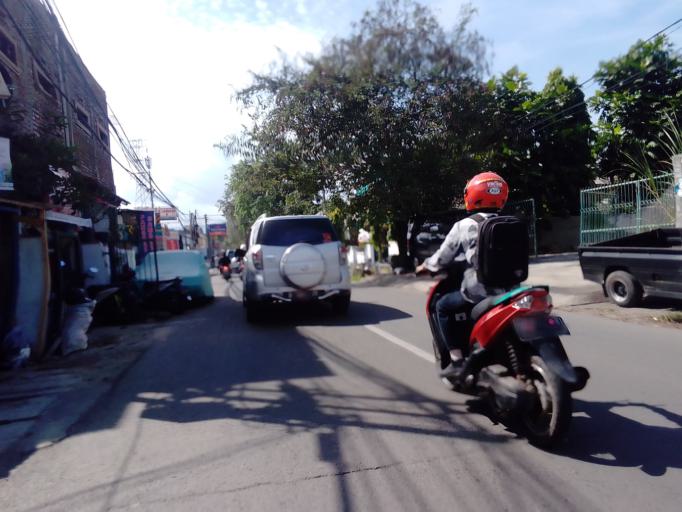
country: ID
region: West Java
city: Bandung
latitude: -6.9420
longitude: 107.6636
